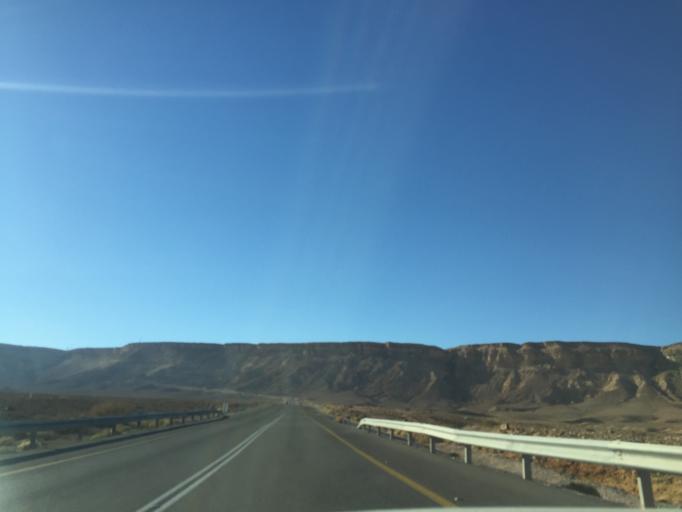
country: IL
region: Southern District
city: Mitzpe Ramon
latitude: 30.6239
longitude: 34.8400
